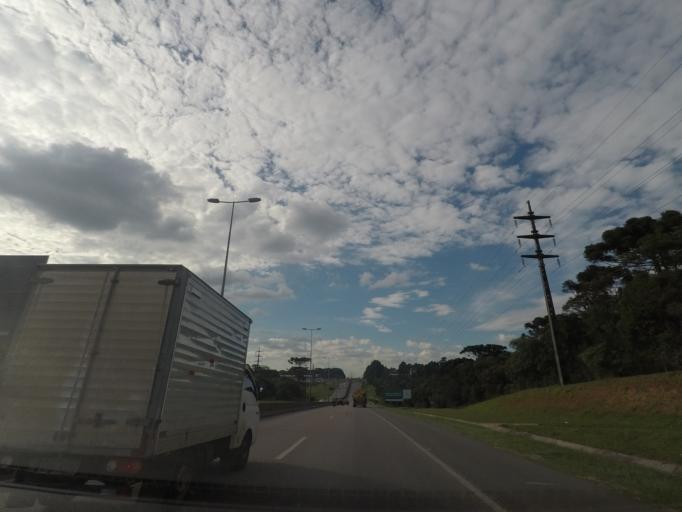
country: BR
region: Parana
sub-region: Araucaria
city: Araucaria
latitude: -25.5846
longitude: -49.3139
